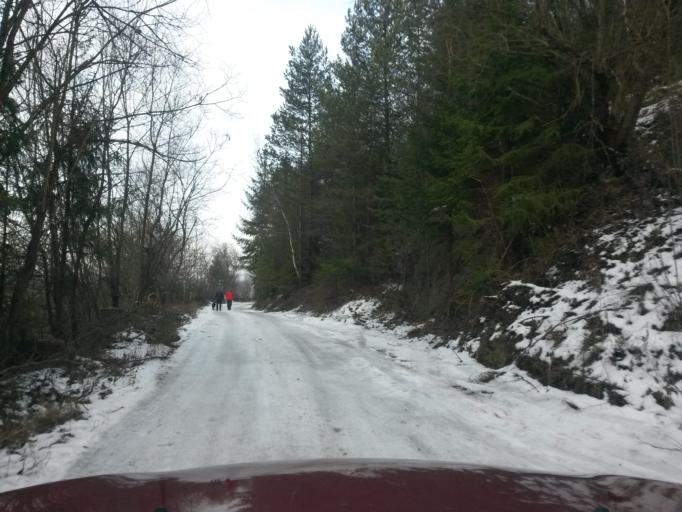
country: SK
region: Kosicky
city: Spisska Nova Ves
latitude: 48.8971
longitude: 20.6443
